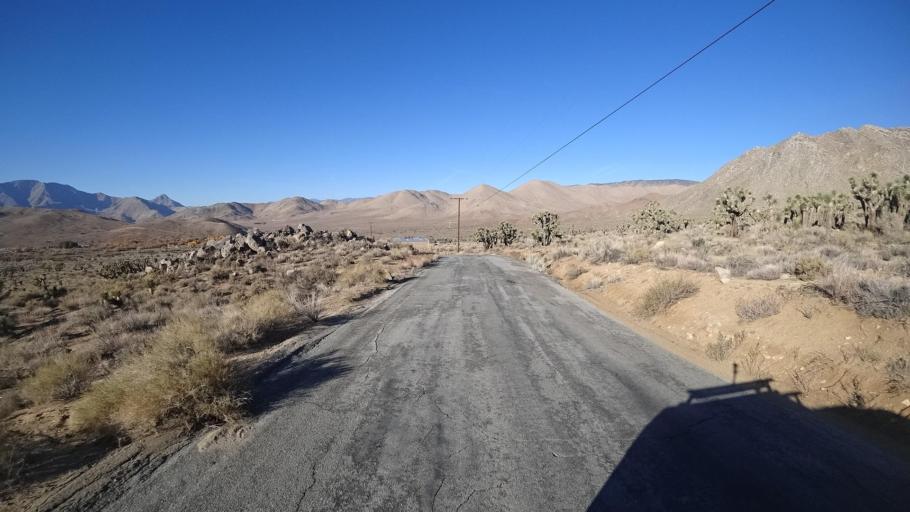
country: US
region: California
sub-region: Kern County
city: Weldon
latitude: 35.5327
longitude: -118.2014
